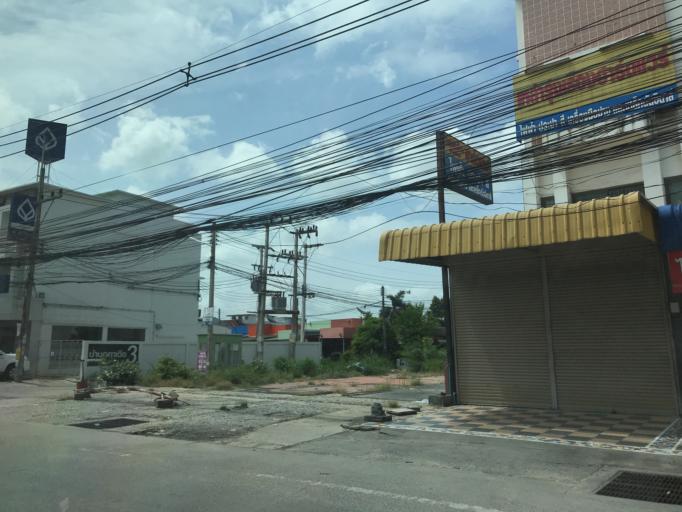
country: TH
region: Chon Buri
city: Si Racha
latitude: 13.1462
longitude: 100.9568
